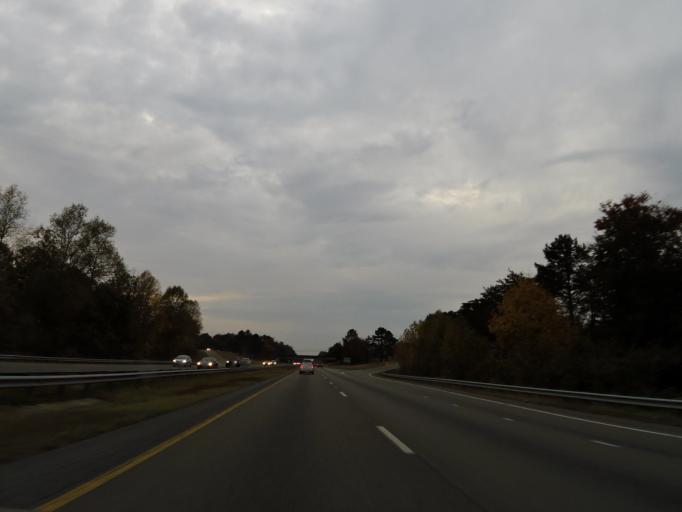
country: US
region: North Carolina
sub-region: Burke County
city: Hildebran
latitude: 35.7085
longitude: -81.4357
